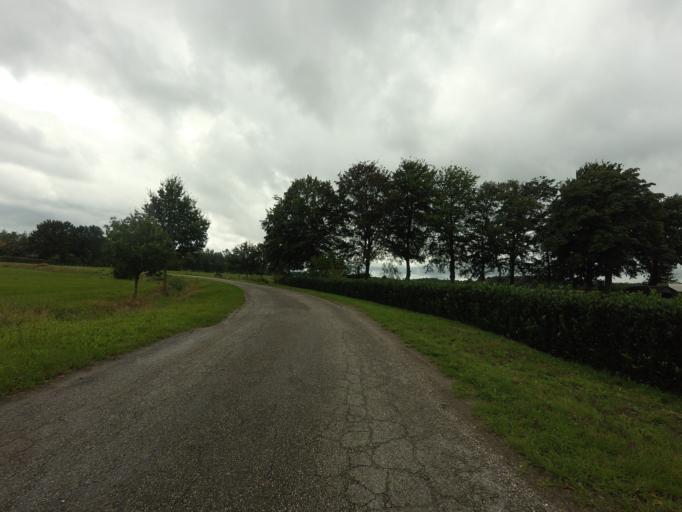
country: NL
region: Friesland
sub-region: Gemeente Weststellingwerf
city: Noordwolde
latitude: 52.9629
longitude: 6.2641
